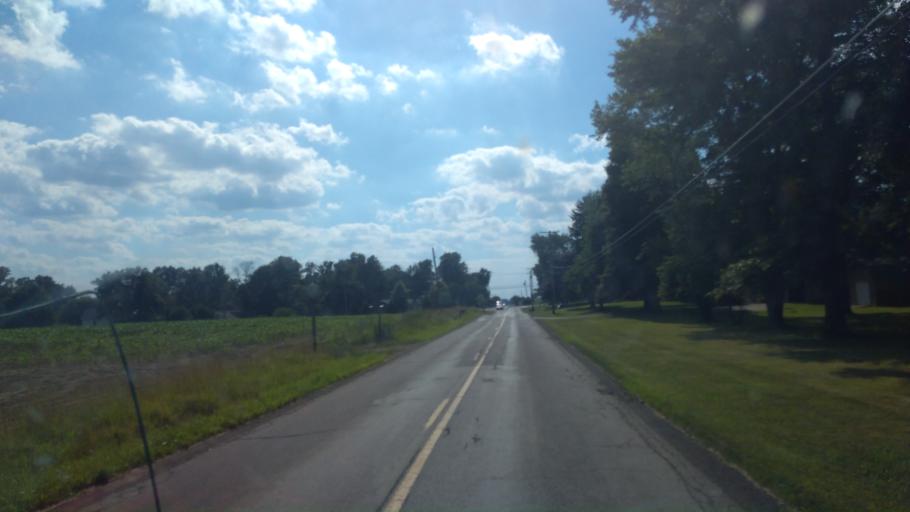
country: US
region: Ohio
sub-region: Wayne County
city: Dalton
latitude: 40.7559
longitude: -81.7429
